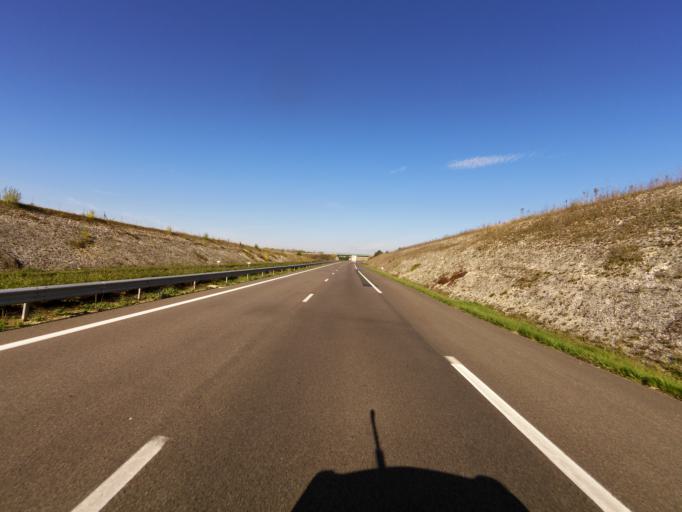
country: FR
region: Champagne-Ardenne
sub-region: Departement de la Marne
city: Fagnieres
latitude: 49.0285
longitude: 4.2855
